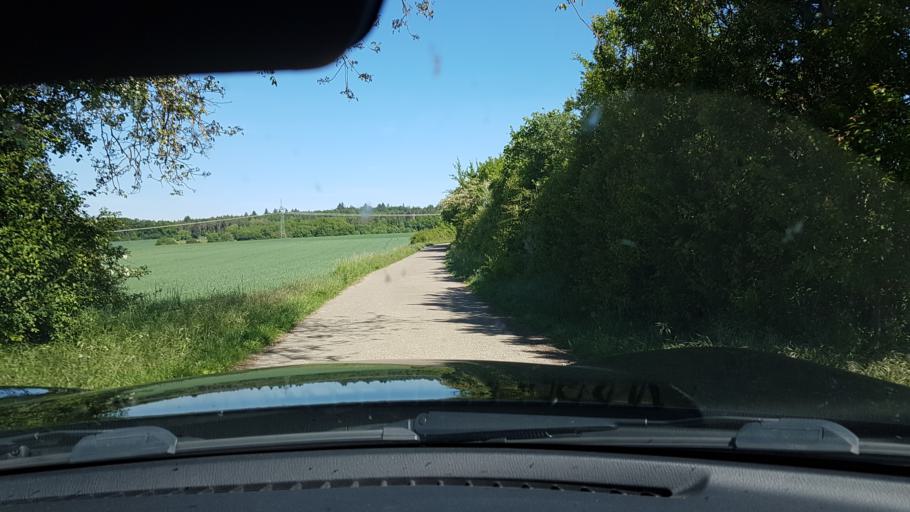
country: DE
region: Baden-Wuerttemberg
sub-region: Karlsruhe Region
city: Osterburken
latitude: 49.4373
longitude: 9.4210
